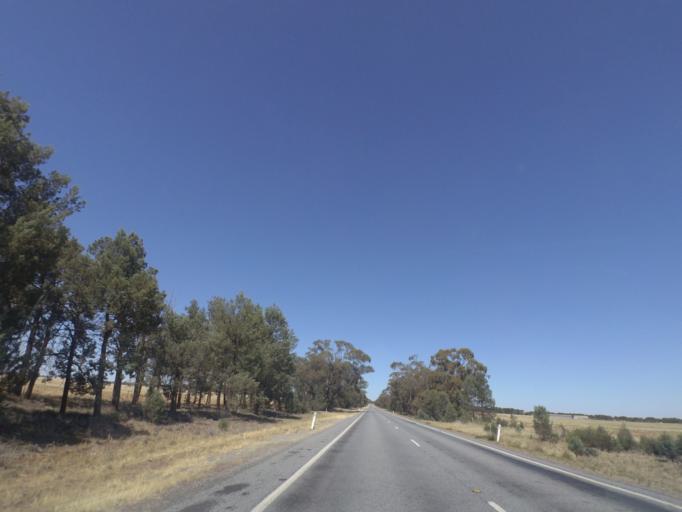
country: AU
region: New South Wales
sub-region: Narrandera
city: Narrandera
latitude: -34.4153
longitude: 146.8616
